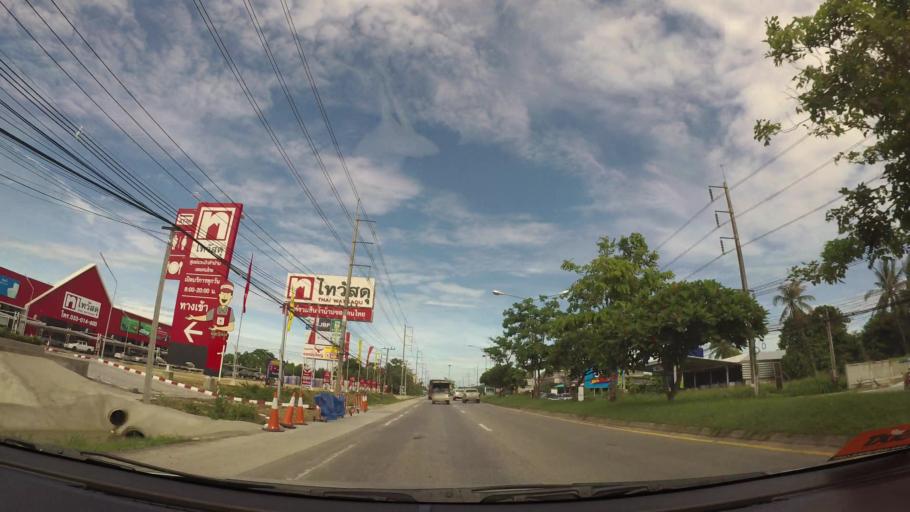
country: TH
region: Rayong
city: Ban Chang
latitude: 12.7353
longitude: 101.0767
